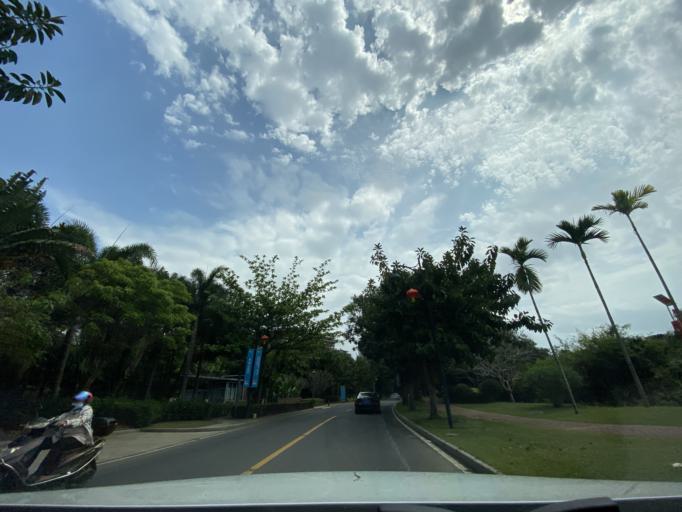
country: CN
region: Hainan
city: Liji
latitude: 18.6695
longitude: 110.2692
